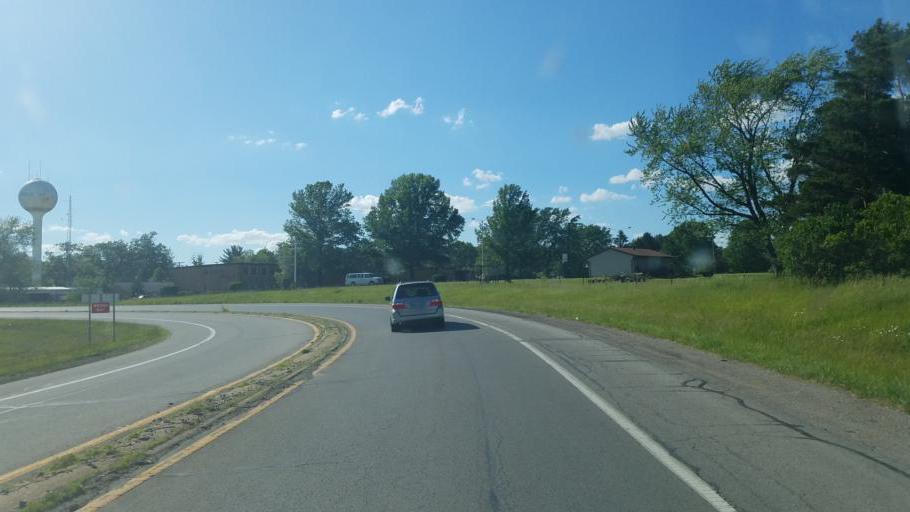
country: US
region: Ohio
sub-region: Richland County
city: Lincoln Heights
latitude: 40.7807
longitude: -82.4705
